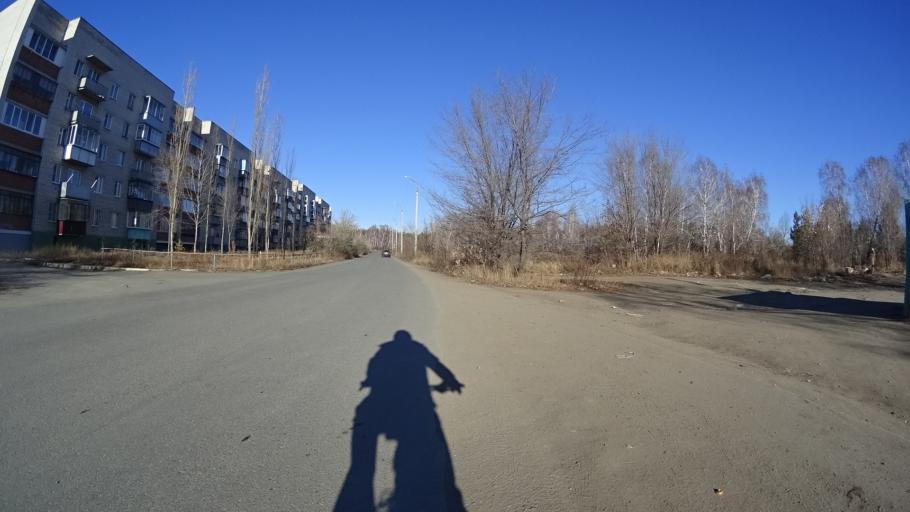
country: RU
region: Chelyabinsk
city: Troitsk
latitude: 54.0515
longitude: 61.6406
